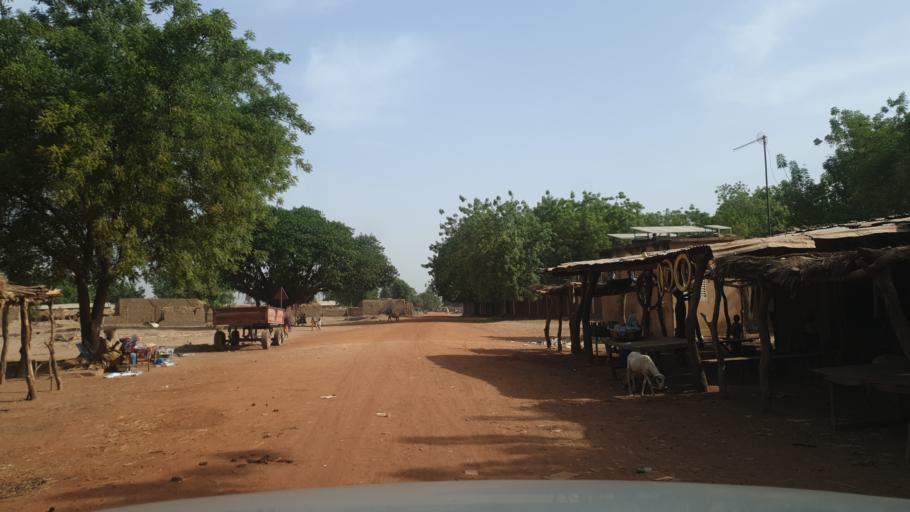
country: ML
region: Koulikoro
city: Kolokani
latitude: 13.3202
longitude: -8.2752
